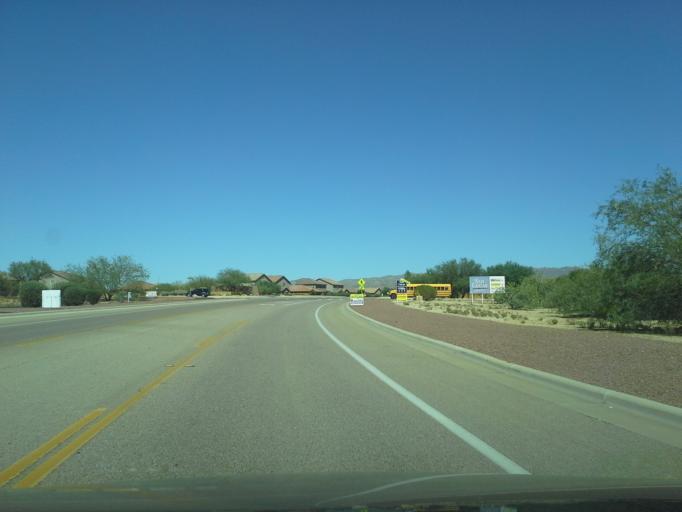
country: US
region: Arizona
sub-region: Pima County
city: Marana
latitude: 32.4642
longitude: -111.2141
